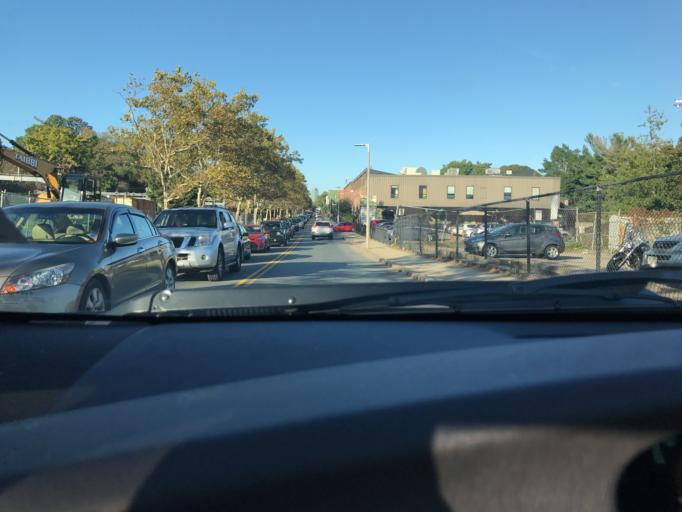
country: US
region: Massachusetts
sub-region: Suffolk County
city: Jamaica Plain
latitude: 42.3075
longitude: -71.1090
